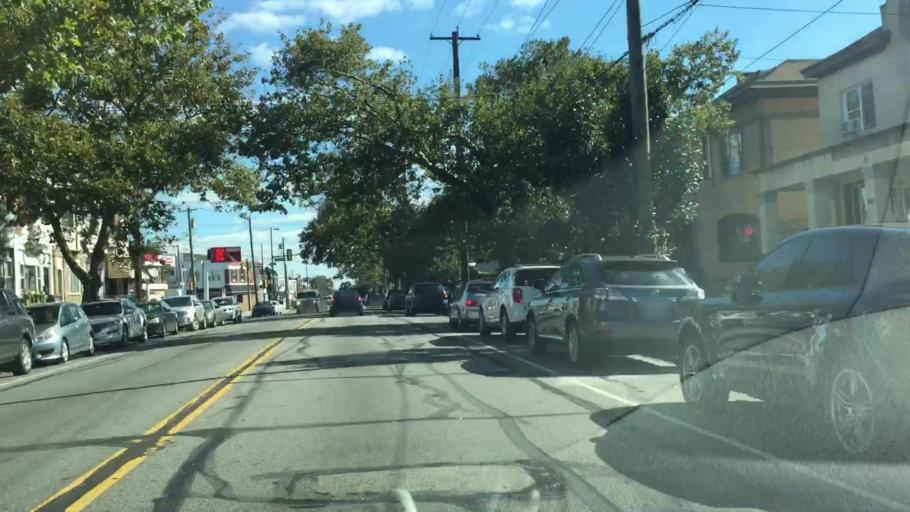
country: US
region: Pennsylvania
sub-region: Philadelphia County
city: Philadelphia
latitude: 39.9230
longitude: -75.1831
